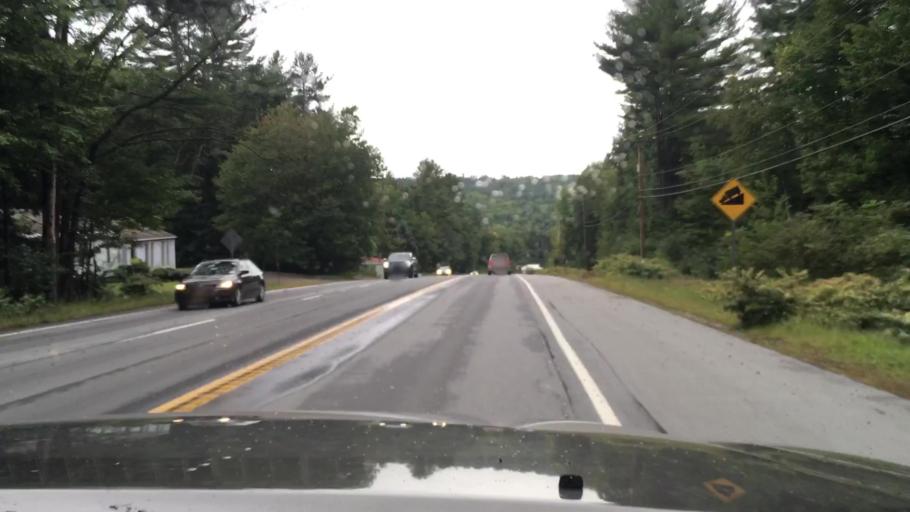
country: US
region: New Hampshire
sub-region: Cheshire County
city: Chesterfield
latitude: 42.8942
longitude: -72.4932
